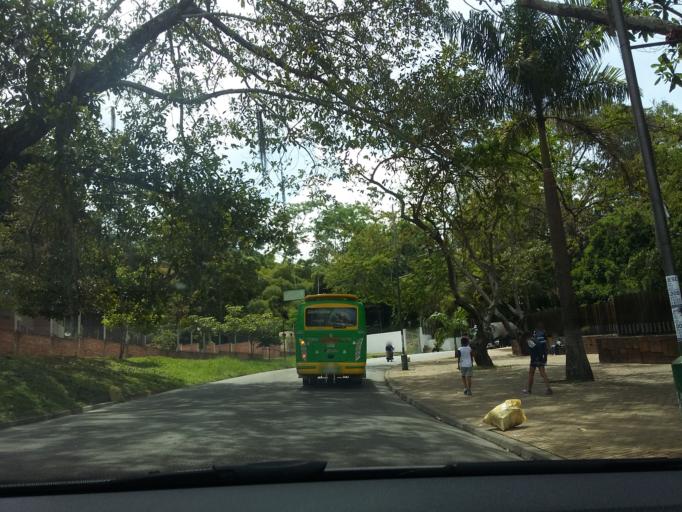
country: CO
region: Santander
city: Bucaramanga
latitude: 7.1312
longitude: -73.1096
